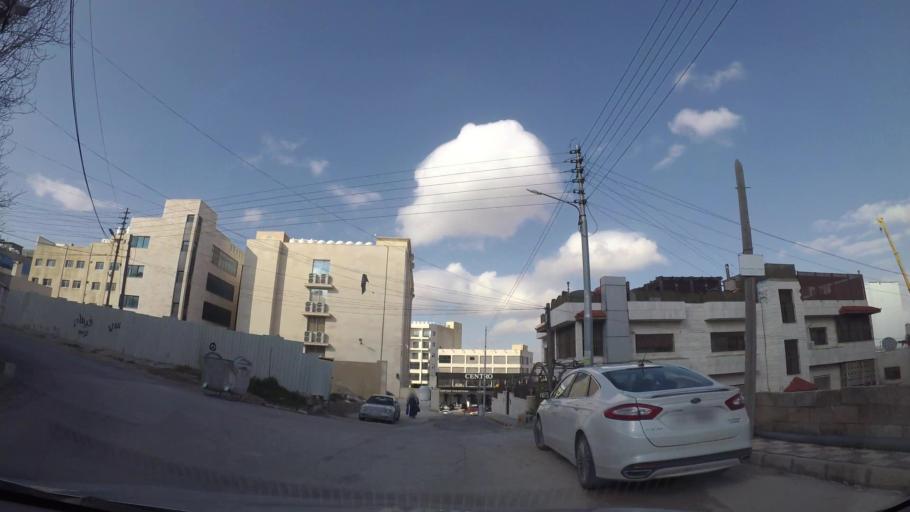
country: JO
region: Amman
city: Al Jubayhah
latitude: 32.0235
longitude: 35.8569
